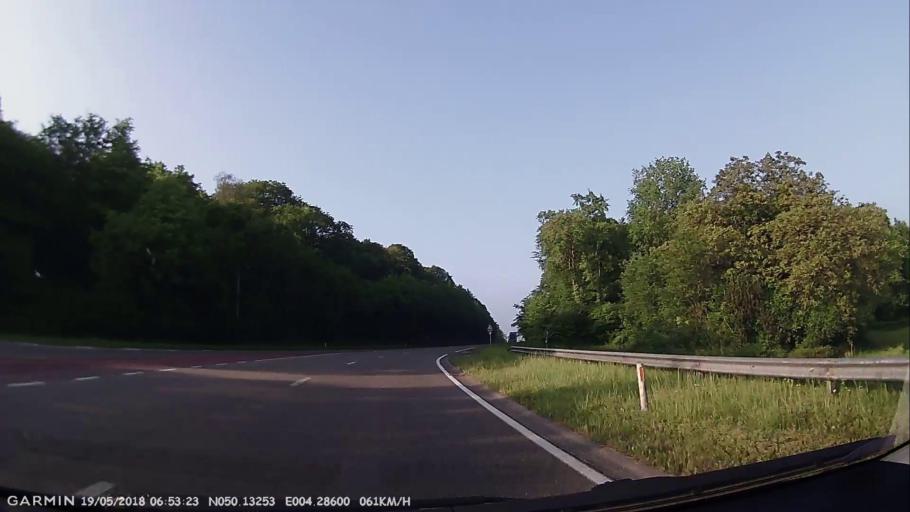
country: BE
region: Wallonia
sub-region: Province du Hainaut
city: Froidchapelle
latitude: 50.1323
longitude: 4.2860
